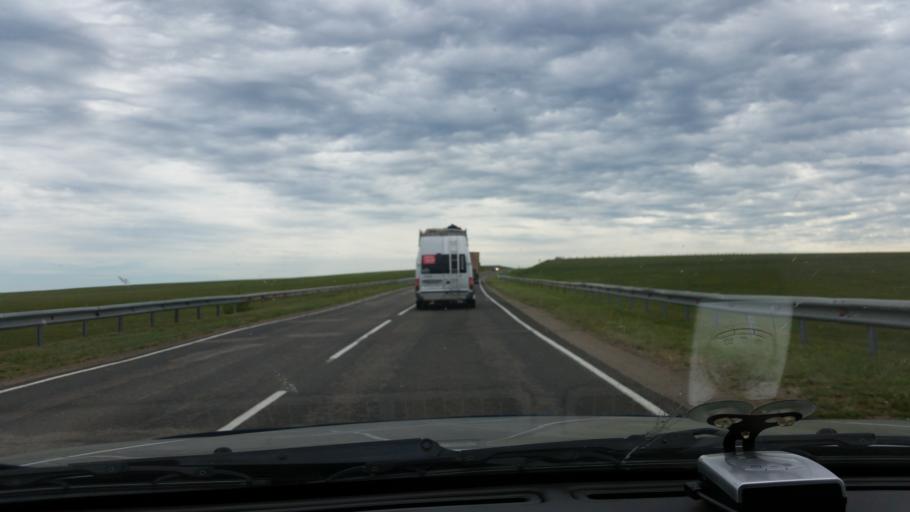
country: RU
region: Irkutsk
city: Ust'-Ordynskiy
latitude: 52.9151
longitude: 105.0331
